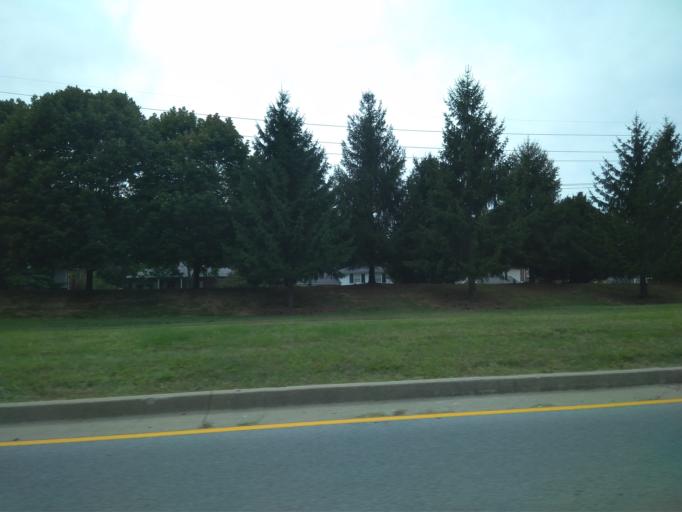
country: US
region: Kentucky
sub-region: Jefferson County
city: Worthington
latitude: 38.2826
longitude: -85.5677
